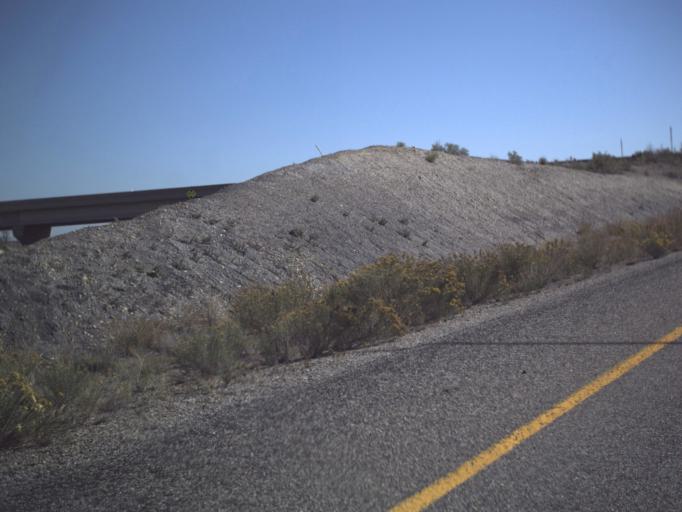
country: US
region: Utah
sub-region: Emery County
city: Castle Dale
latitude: 39.1752
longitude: -111.0480
